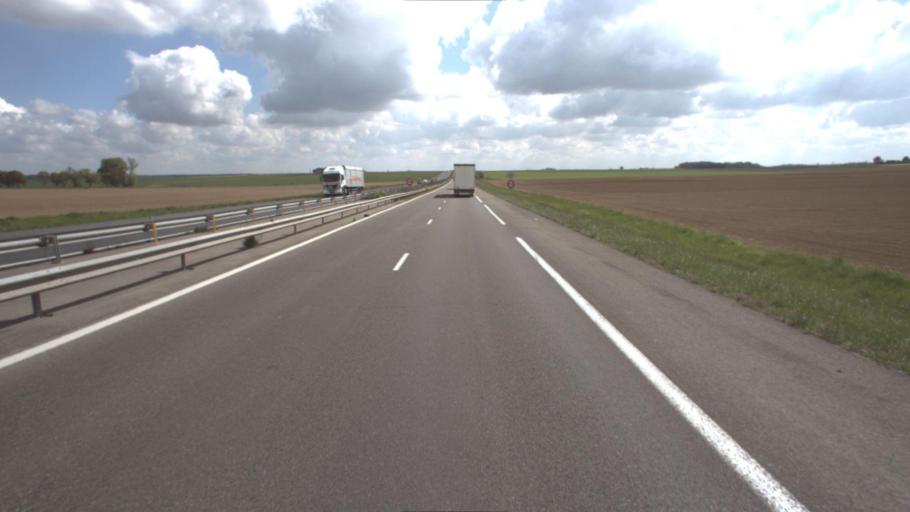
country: FR
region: Ile-de-France
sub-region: Departement de Seine-et-Marne
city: Touquin
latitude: 48.6854
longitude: 3.0305
